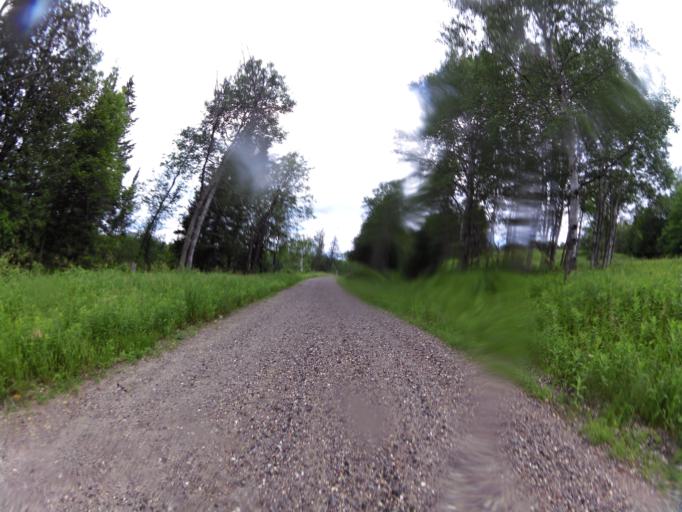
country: CA
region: Ontario
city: Renfrew
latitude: 45.0740
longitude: -76.7411
